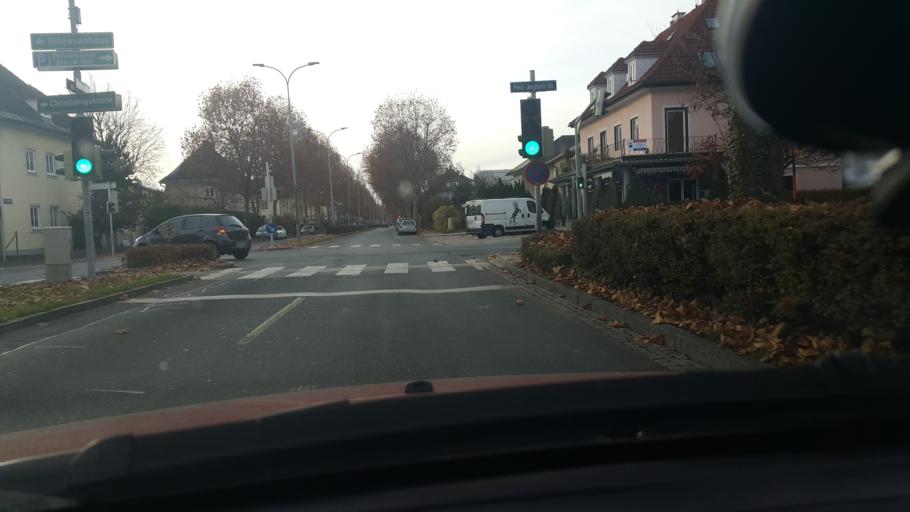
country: AT
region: Carinthia
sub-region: Klagenfurt am Woerthersee
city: Klagenfurt am Woerthersee
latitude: 46.6248
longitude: 14.2959
